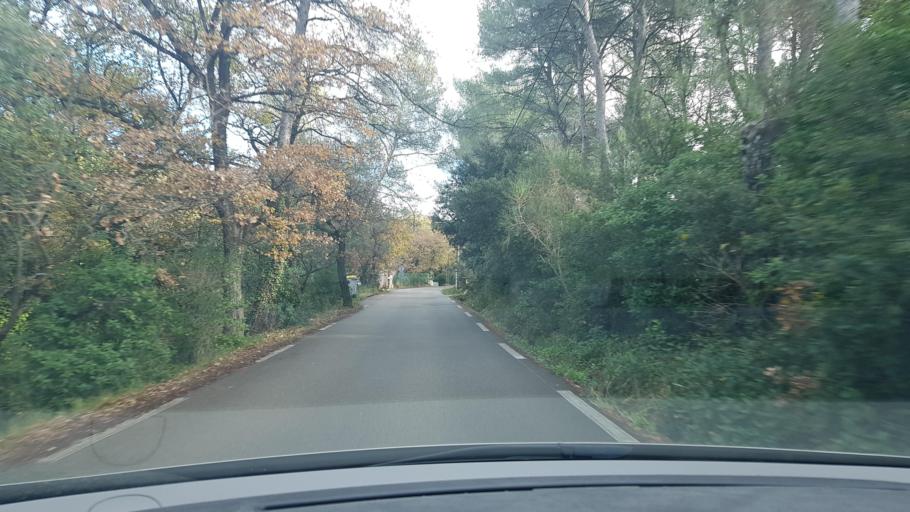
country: FR
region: Provence-Alpes-Cote d'Azur
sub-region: Departement des Bouches-du-Rhone
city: Simiane-Collongue
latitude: 43.4203
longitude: 5.4568
